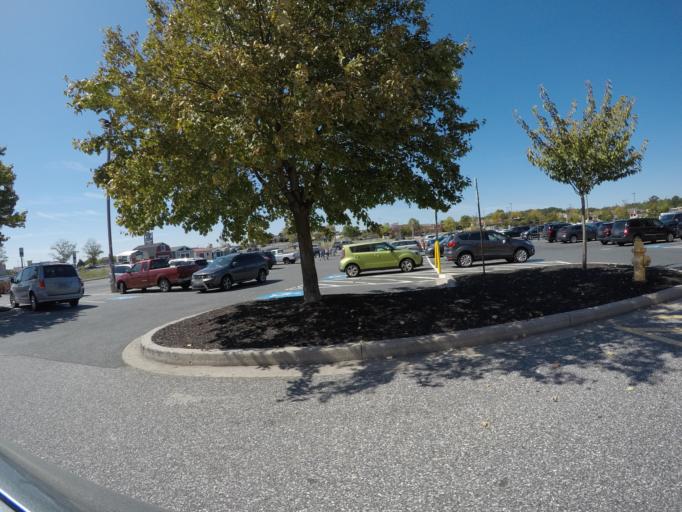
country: US
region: Maryland
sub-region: Harford County
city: Aberdeen
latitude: 39.5235
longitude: -76.1811
